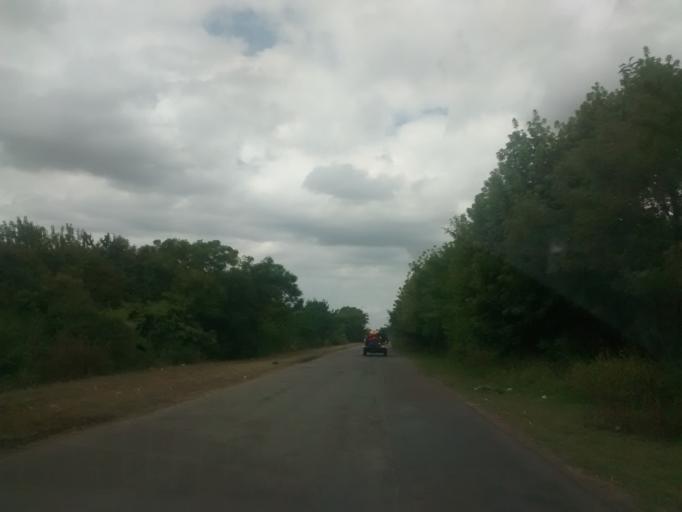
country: AR
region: Buenos Aires
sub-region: Partido de La Plata
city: La Plata
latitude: -34.9778
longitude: -57.9345
